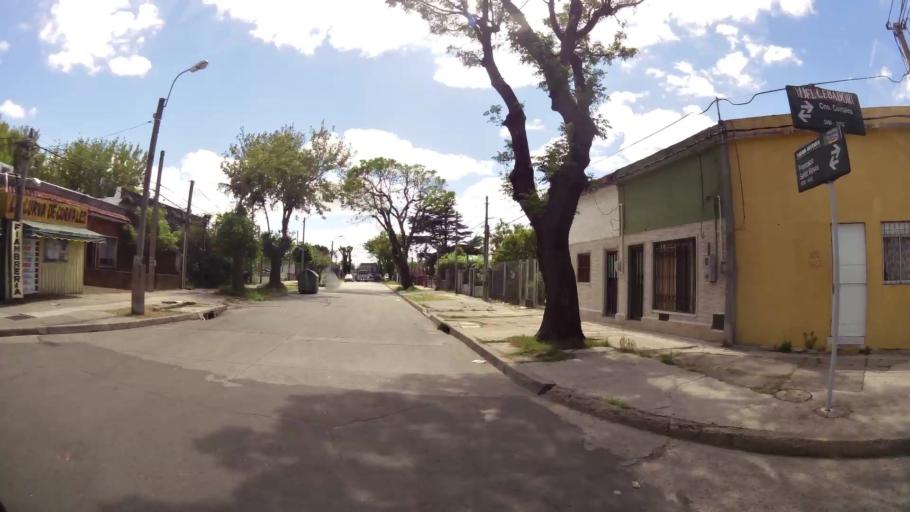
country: UY
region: Montevideo
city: Montevideo
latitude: -34.8535
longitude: -56.1444
